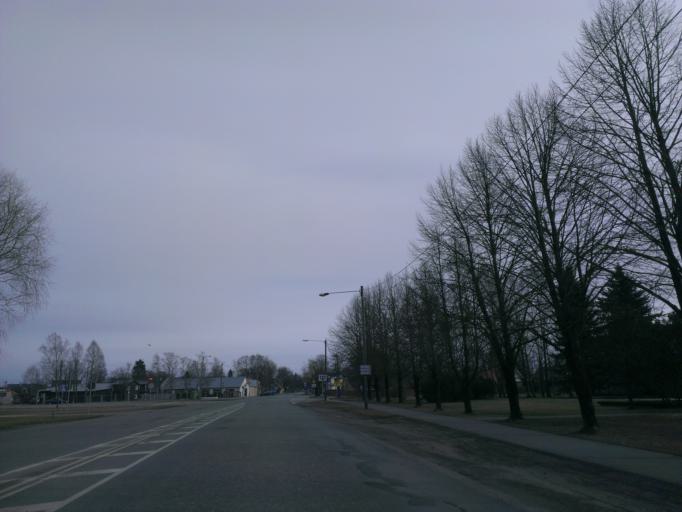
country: EE
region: Paernumaa
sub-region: Paernu linn
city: Parnu
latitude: 58.3937
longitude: 24.4602
